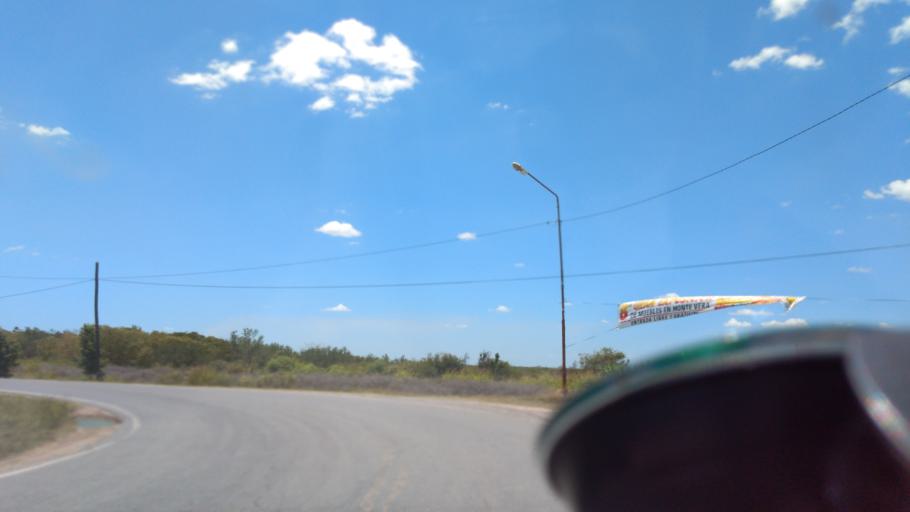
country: AR
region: Santa Fe
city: Laguna Paiva
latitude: -31.3271
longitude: -60.6593
